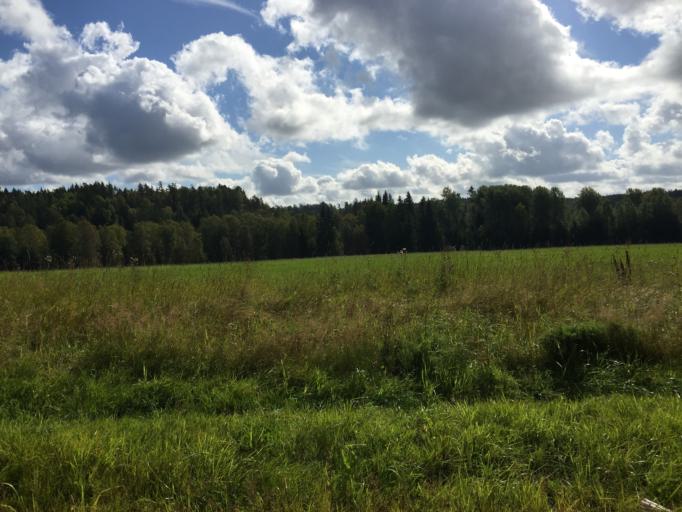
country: SE
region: Stockholm
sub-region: Botkyrka Kommun
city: Tullinge
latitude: 59.1647
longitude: 17.8968
